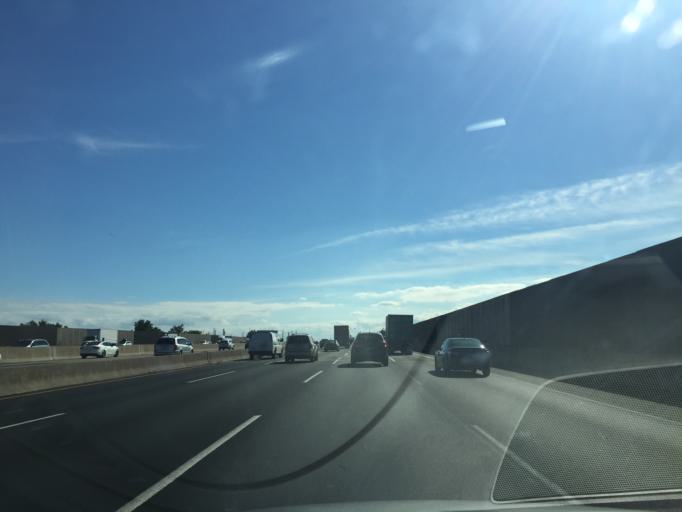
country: US
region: New Jersey
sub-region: Union County
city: Elizabeth
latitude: 40.6542
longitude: -74.1923
